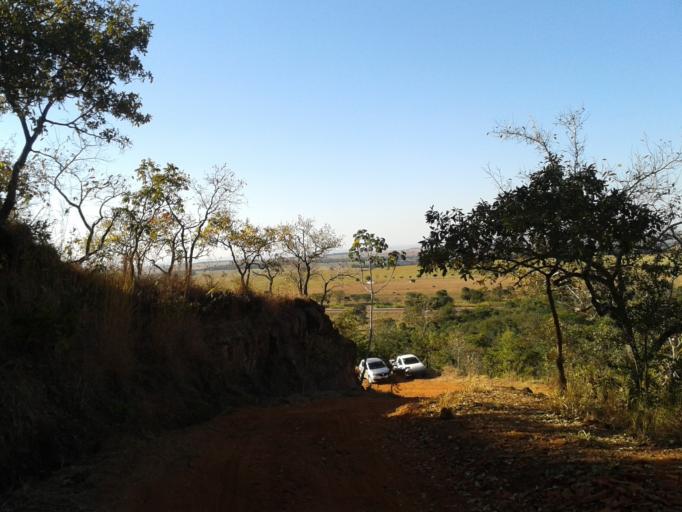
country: BR
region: Minas Gerais
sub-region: Capinopolis
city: Capinopolis
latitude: -18.7600
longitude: -49.5380
